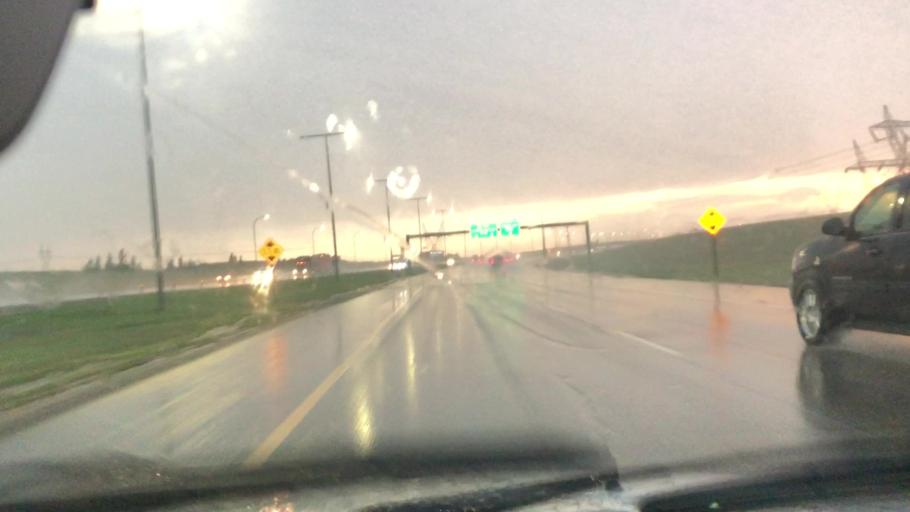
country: CA
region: Alberta
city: Edmonton
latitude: 53.4286
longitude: -113.5669
